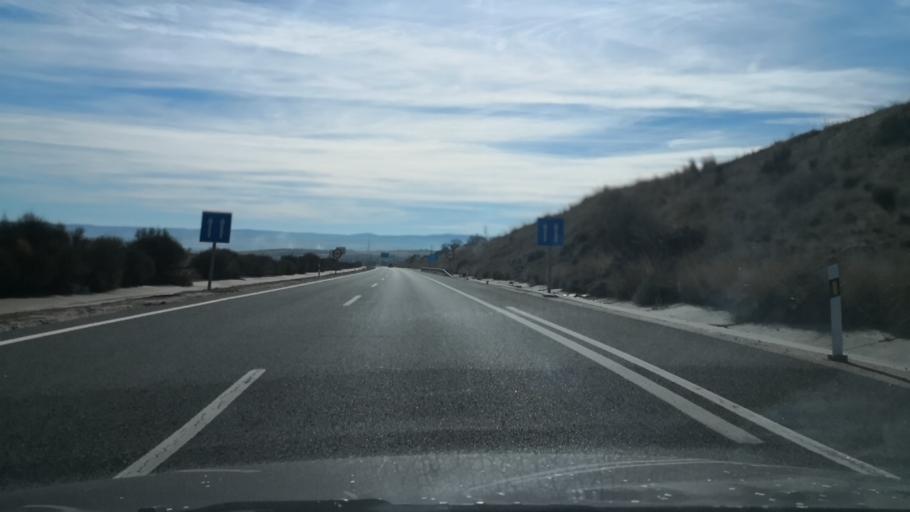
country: ES
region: Castille and Leon
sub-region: Provincia de Avila
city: Martiherrero
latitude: 40.6916
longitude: -4.7387
